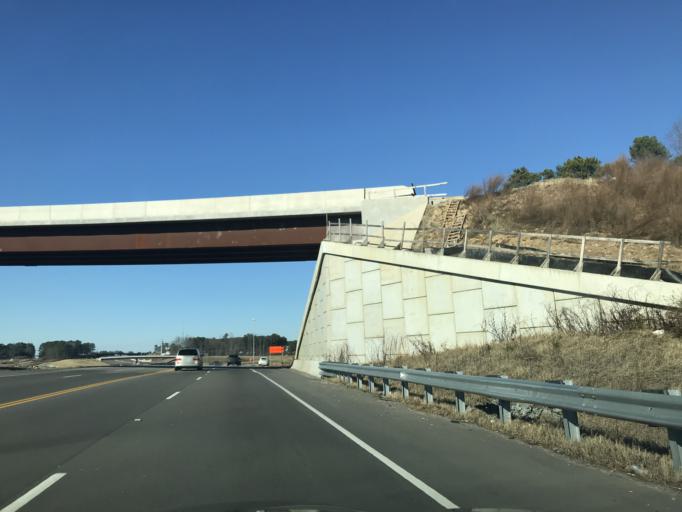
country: US
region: North Carolina
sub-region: Durham County
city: Durham
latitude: 35.9758
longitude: -78.8535
